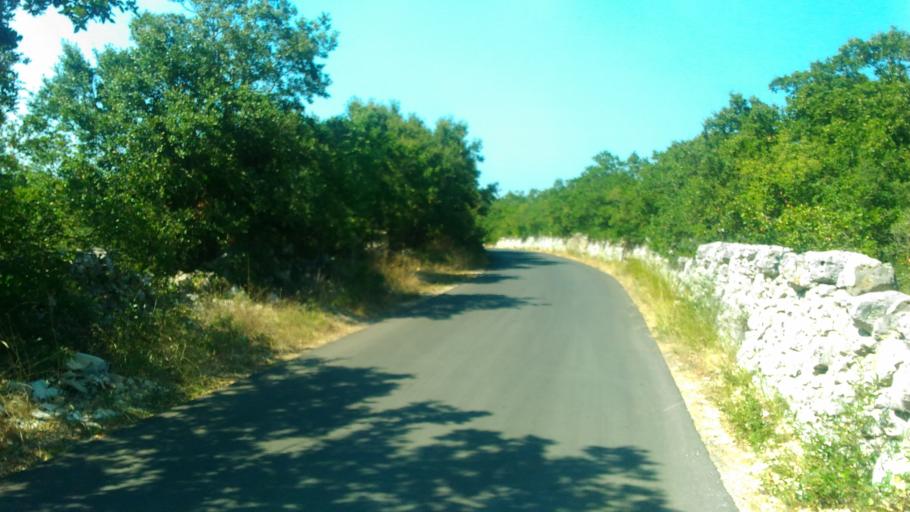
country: IT
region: Apulia
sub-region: Provincia di Bari
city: Alberobello
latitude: 40.8060
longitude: 17.1831
